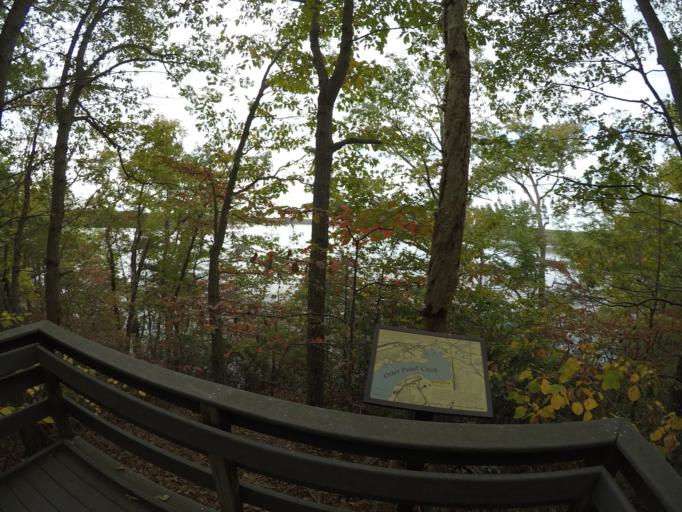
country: US
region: Maryland
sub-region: Harford County
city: Riverside
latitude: 39.4496
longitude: -76.2695
